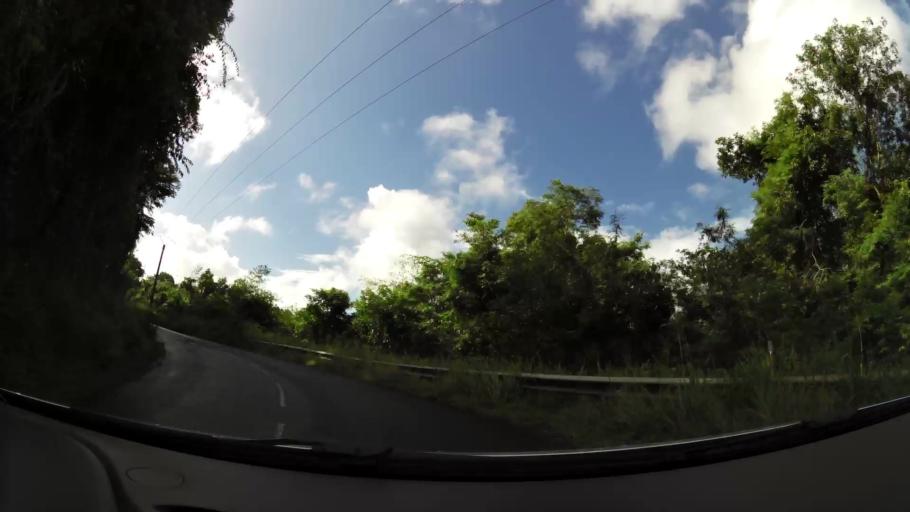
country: MQ
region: Martinique
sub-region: Martinique
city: Les Trois-Ilets
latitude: 14.5274
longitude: -61.0753
